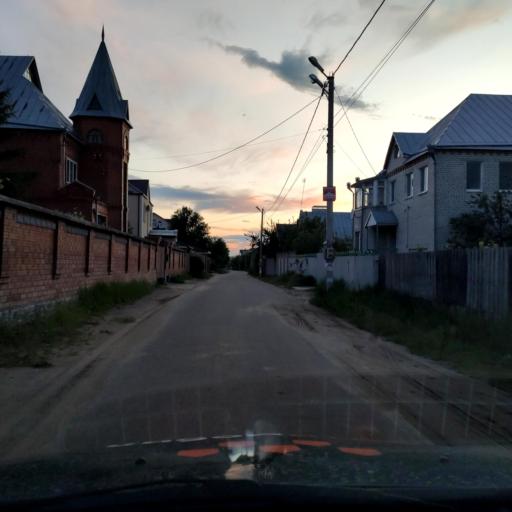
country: RU
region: Voronezj
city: Podgornoye
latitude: 51.7466
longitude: 39.1579
